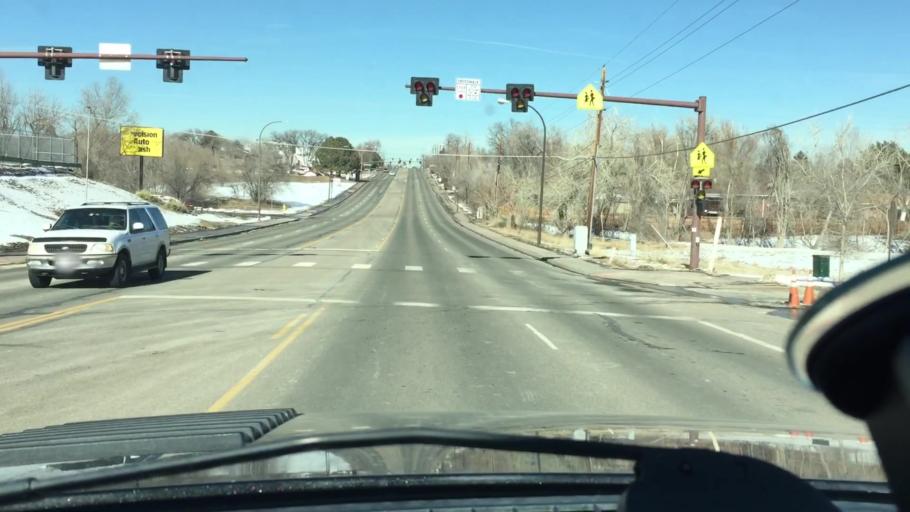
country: US
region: Colorado
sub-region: Adams County
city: Federal Heights
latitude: 39.8503
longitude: -104.9966
